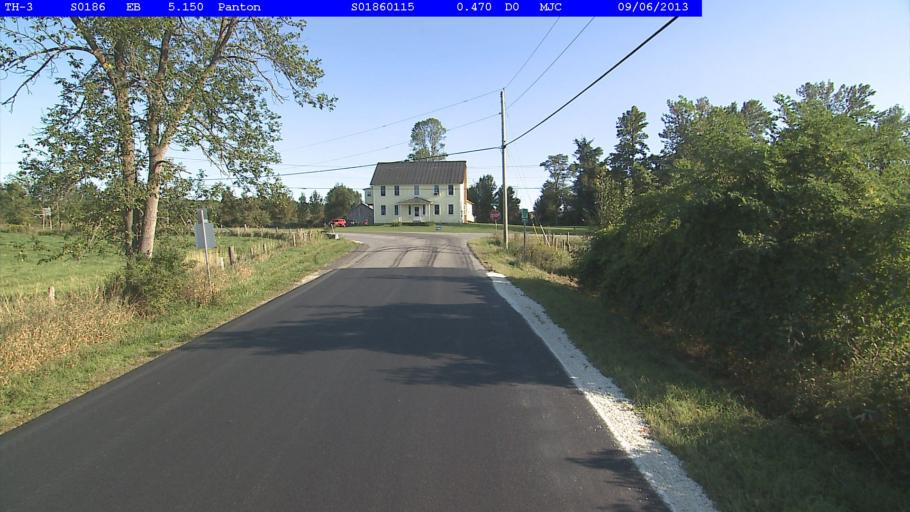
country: US
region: Vermont
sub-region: Addison County
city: Vergennes
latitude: 44.1588
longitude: -73.2859
